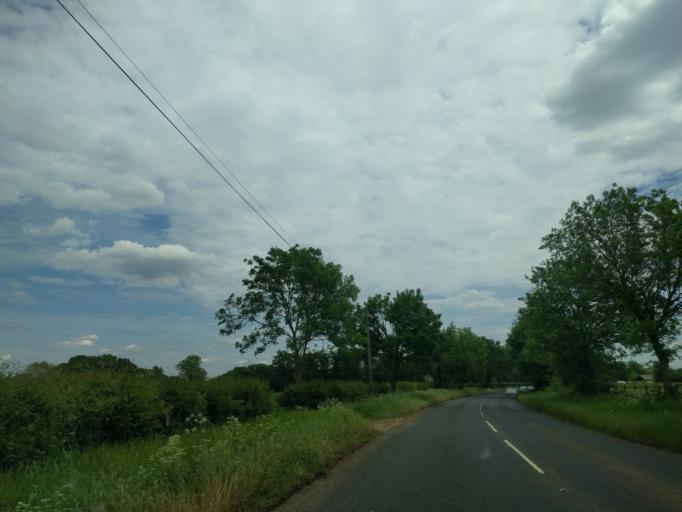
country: GB
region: England
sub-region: Wiltshire
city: Chippenham
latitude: 51.5141
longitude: -2.1088
